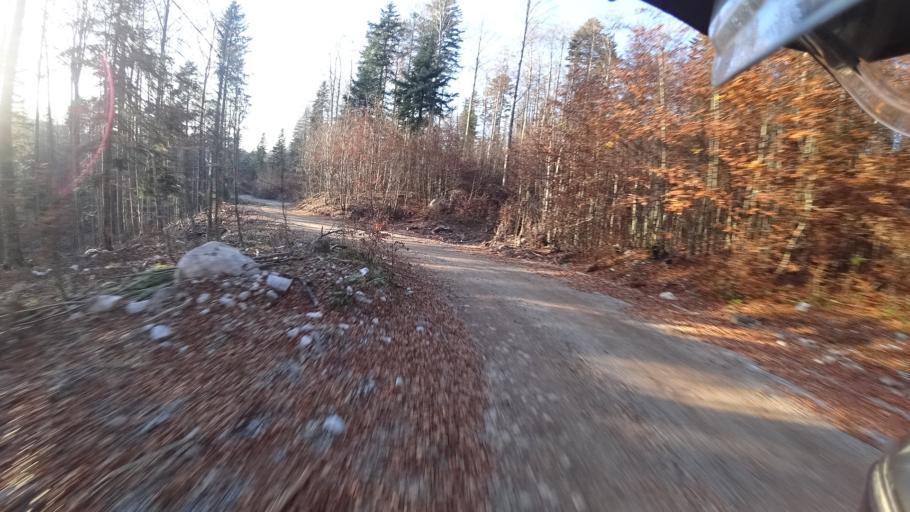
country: HR
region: Primorsko-Goranska
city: Drazice
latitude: 45.4932
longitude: 14.4712
